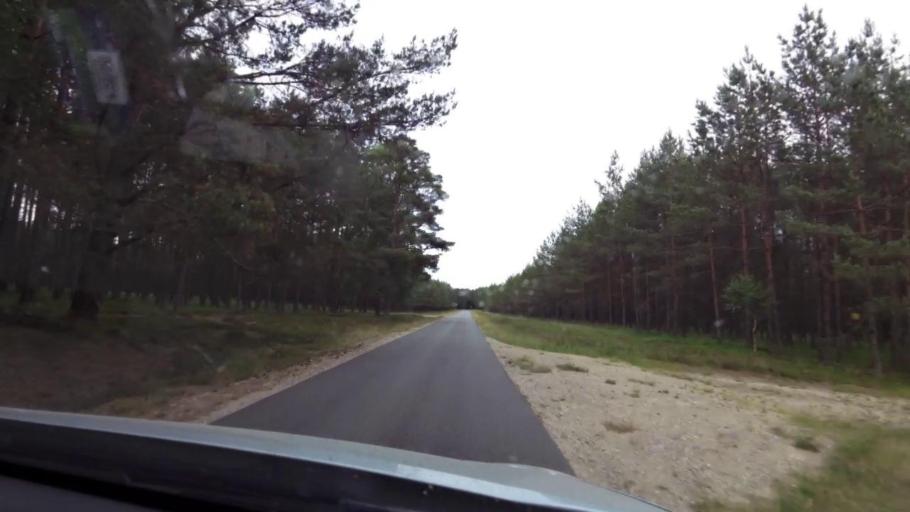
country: PL
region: Pomeranian Voivodeship
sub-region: Powiat bytowski
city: Trzebielino
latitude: 54.1964
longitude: 17.0365
